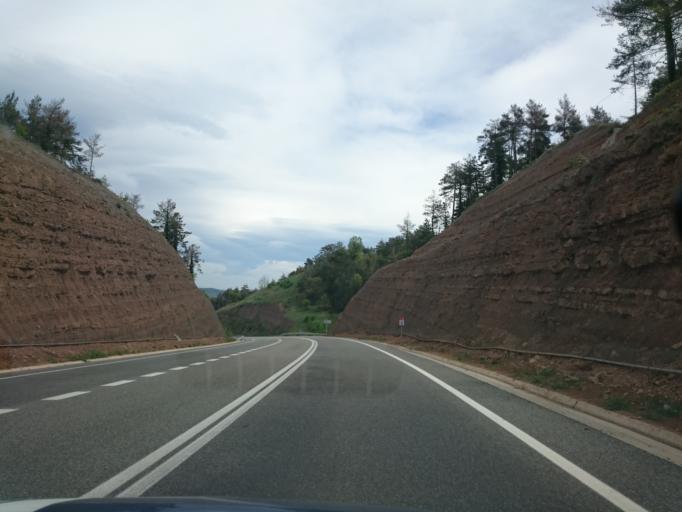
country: ES
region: Catalonia
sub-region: Provincia de Barcelona
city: Olost
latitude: 41.9659
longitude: 2.1310
